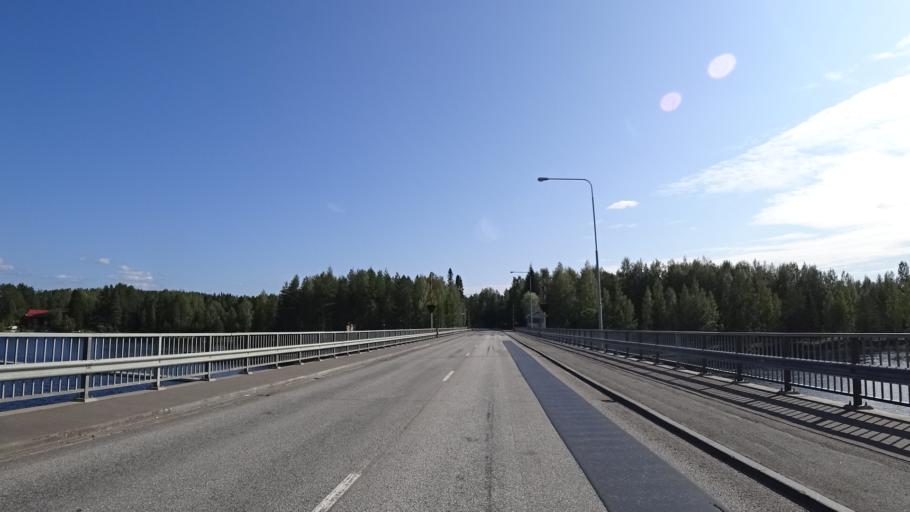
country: FI
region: North Karelia
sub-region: Joensuu
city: Eno
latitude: 62.8032
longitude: 30.1534
